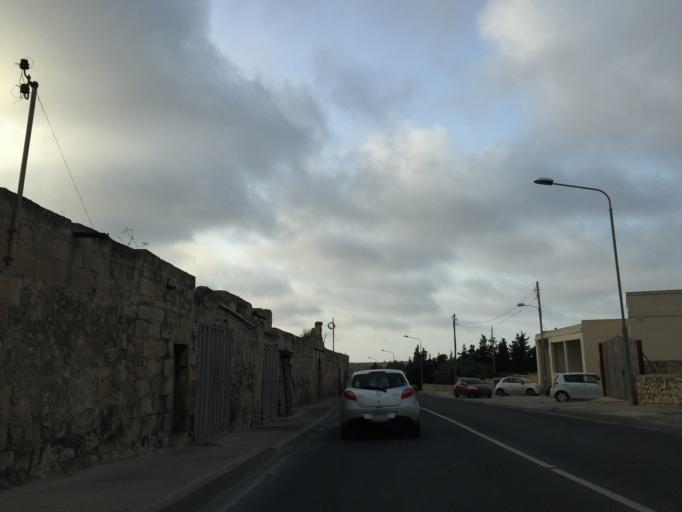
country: MT
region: L-Imtarfa
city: Imtarfa
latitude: 35.8959
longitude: 14.4096
